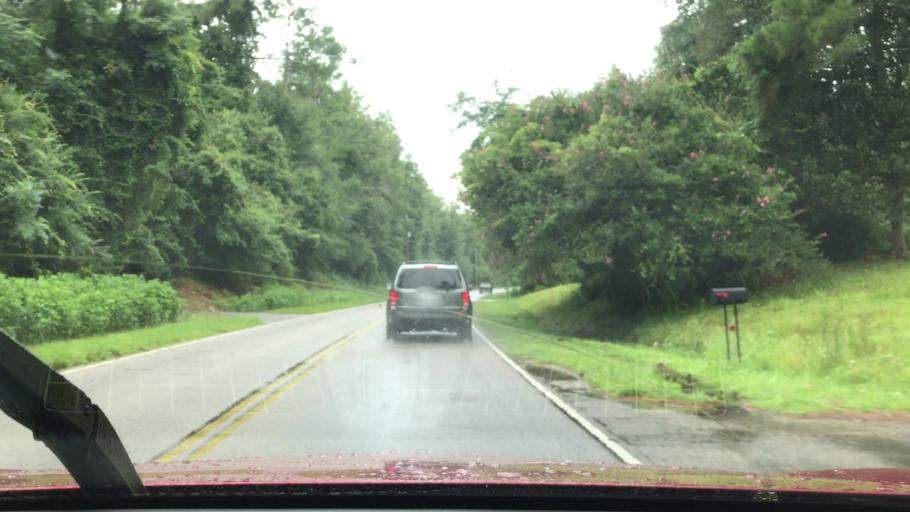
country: US
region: South Carolina
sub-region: Horry County
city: Conway
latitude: 33.8408
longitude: -79.0314
